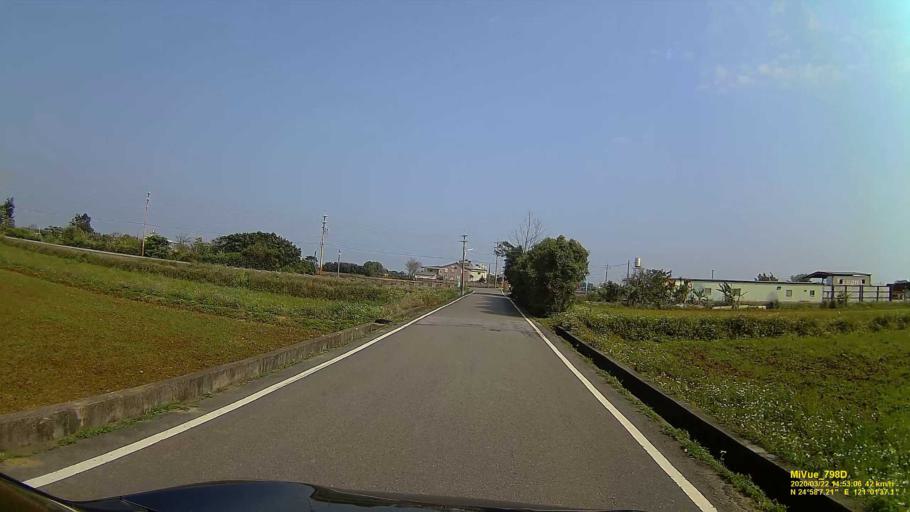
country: TW
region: Taiwan
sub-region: Hsinchu
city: Zhubei
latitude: 24.9686
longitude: 121.0272
